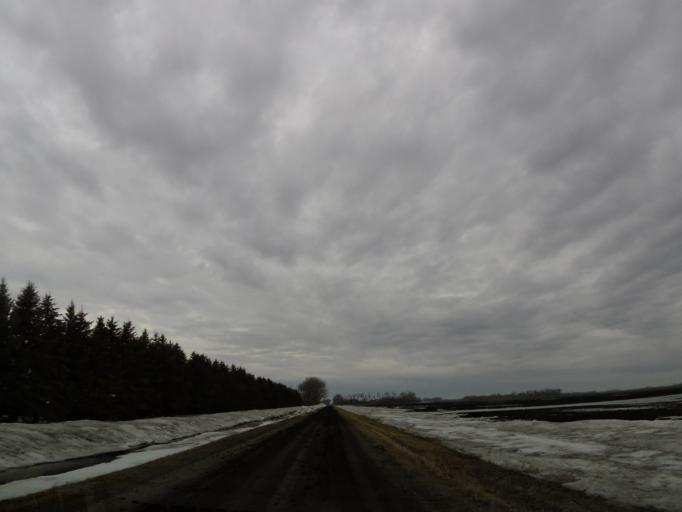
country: US
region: North Dakota
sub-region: Walsh County
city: Grafton
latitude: 48.3836
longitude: -97.4633
